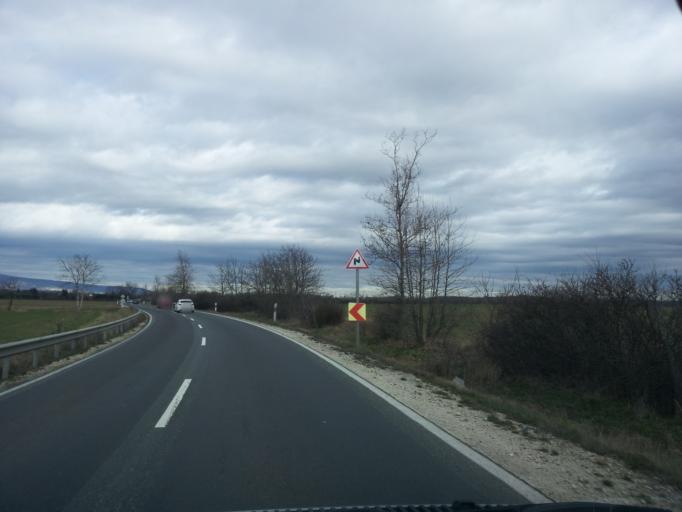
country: HU
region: Vas
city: Gencsapati
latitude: 47.3094
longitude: 16.5950
